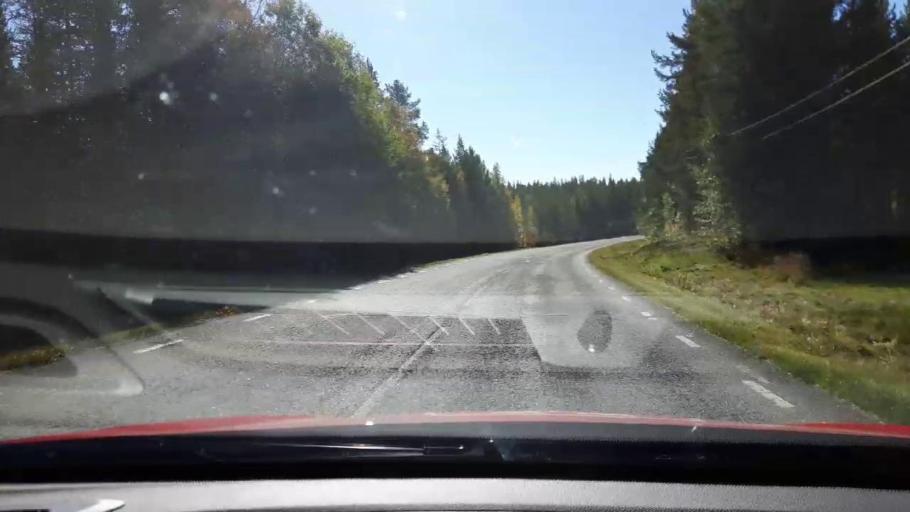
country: SE
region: Jaemtland
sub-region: Harjedalens Kommun
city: Sveg
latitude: 62.3256
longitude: 14.0615
